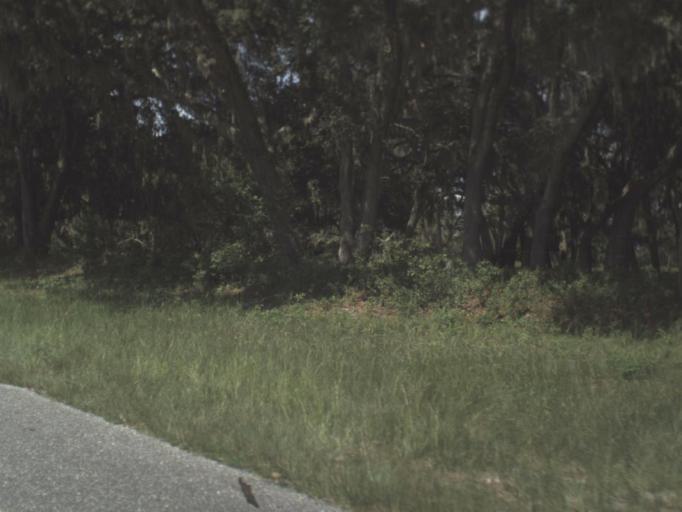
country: US
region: Florida
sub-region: Gilchrist County
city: Trenton
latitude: 29.7395
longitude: -82.7407
